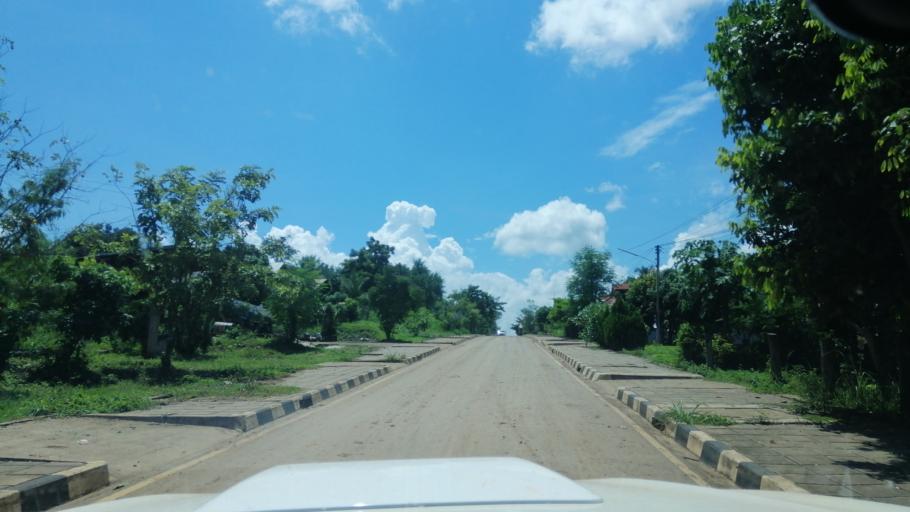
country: TH
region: Uttaradit
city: Ban Khok
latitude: 18.1365
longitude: 101.2824
